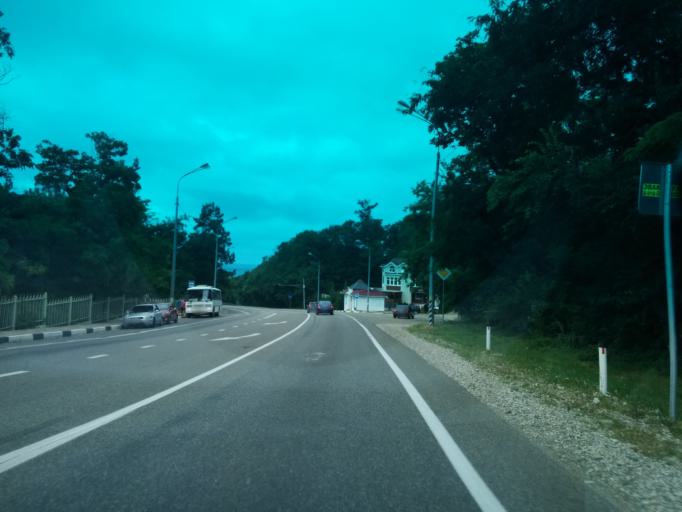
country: RU
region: Krasnodarskiy
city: Nebug
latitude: 44.1773
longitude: 38.9474
